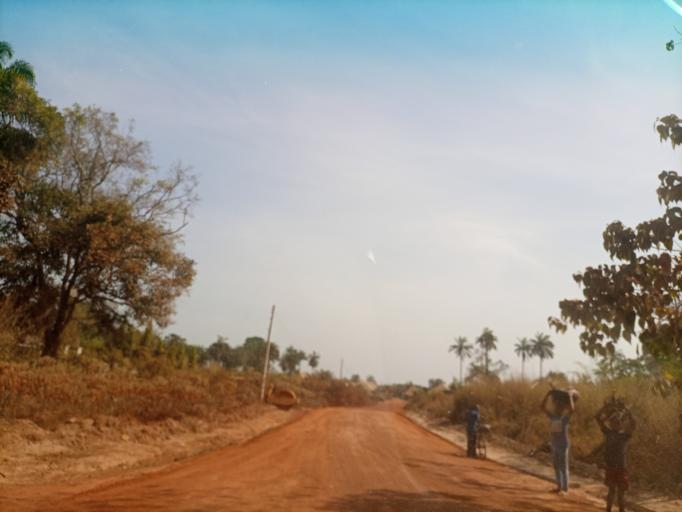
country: NG
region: Enugu
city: Eha Amufu
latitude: 6.6655
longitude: 7.7551
